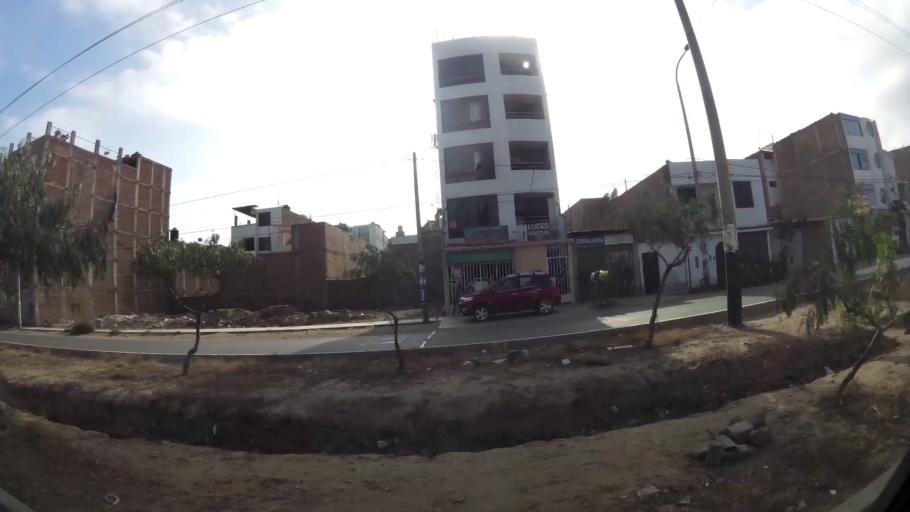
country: PE
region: La Libertad
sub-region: Provincia de Trujillo
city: La Esperanza
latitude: -8.0920
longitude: -79.0476
